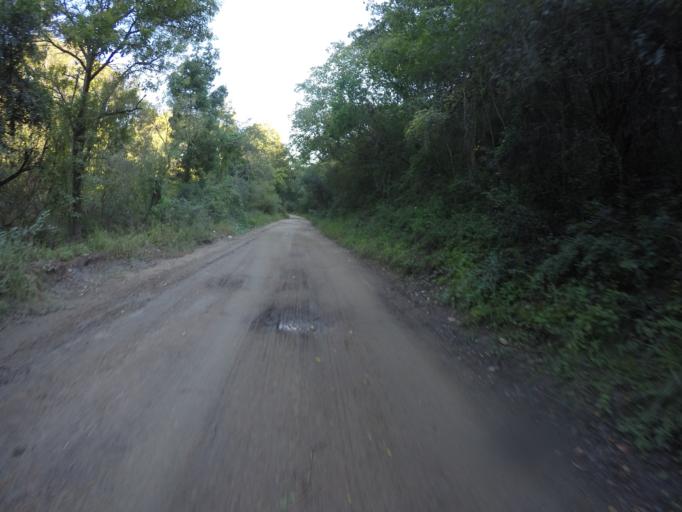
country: ZA
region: Eastern Cape
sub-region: Cacadu District Municipality
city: Kareedouw
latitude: -33.6584
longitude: 24.5308
